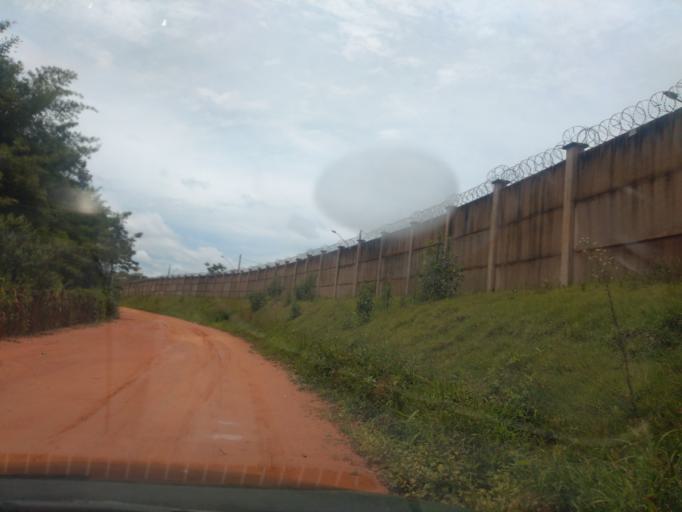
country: BR
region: Minas Gerais
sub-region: Tres Coracoes
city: Tres Coracoes
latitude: -21.6774
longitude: -45.2577
